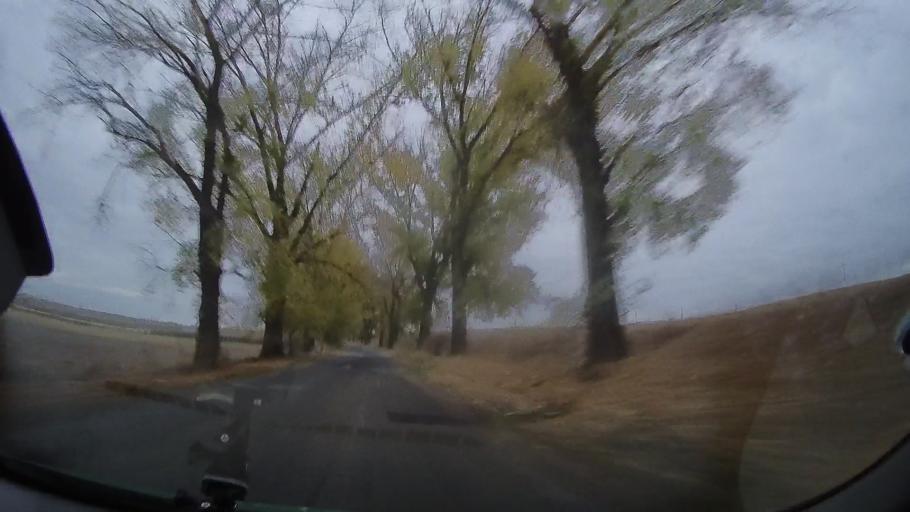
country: RO
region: Tulcea
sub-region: Comuna Mihai Bravu
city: Mihai Bravu
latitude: 44.9626
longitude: 28.6392
